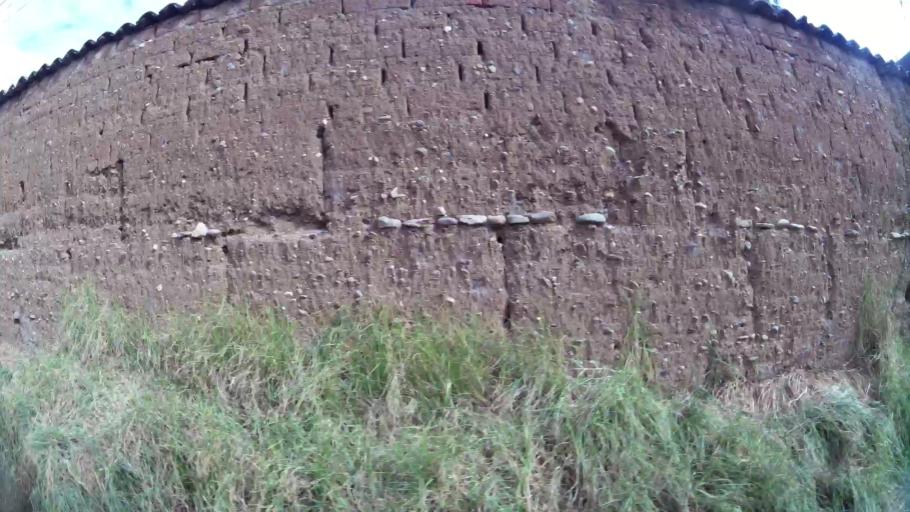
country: PE
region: Junin
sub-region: Provincia de Huancayo
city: Huancayo
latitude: -12.0535
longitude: -75.1985
